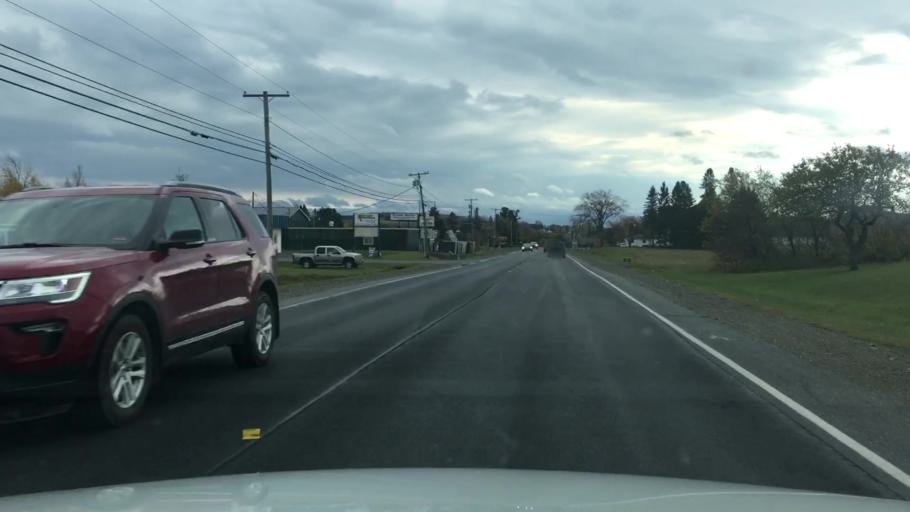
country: US
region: Maine
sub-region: Aroostook County
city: Presque Isle
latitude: 46.6577
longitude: -68.0068
